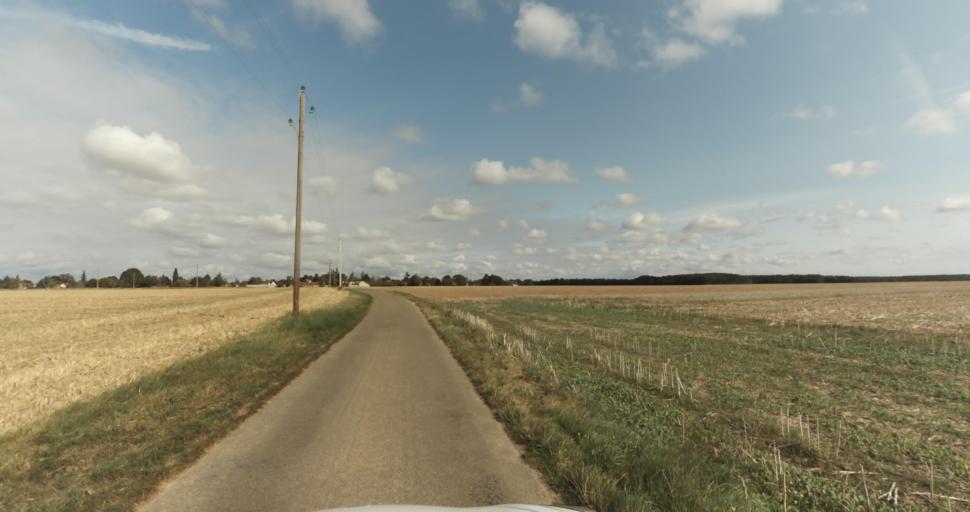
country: FR
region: Haute-Normandie
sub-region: Departement de l'Eure
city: Tillieres-sur-Avre
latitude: 48.7522
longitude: 1.1125
